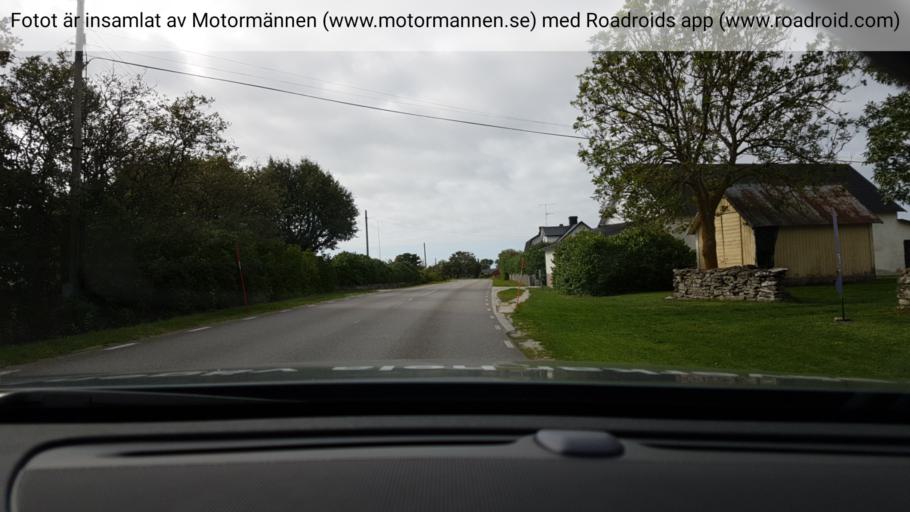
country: SE
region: Gotland
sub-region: Gotland
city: Hemse
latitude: 56.9688
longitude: 18.2316
